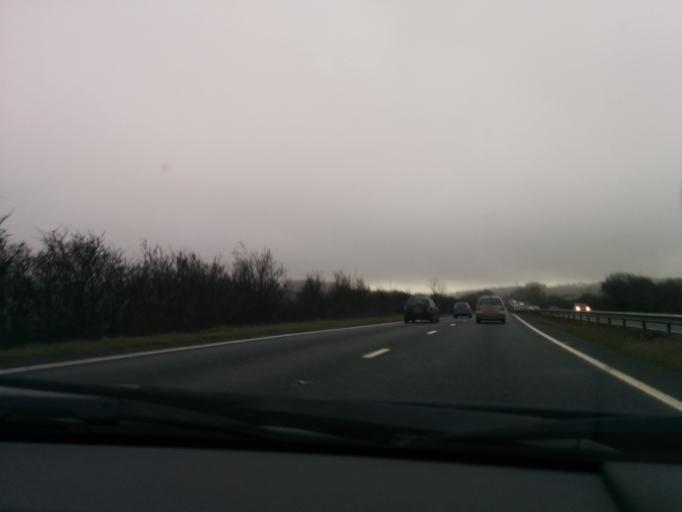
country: GB
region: England
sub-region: Hampshire
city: Highclere
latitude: 51.3096
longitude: -1.3336
